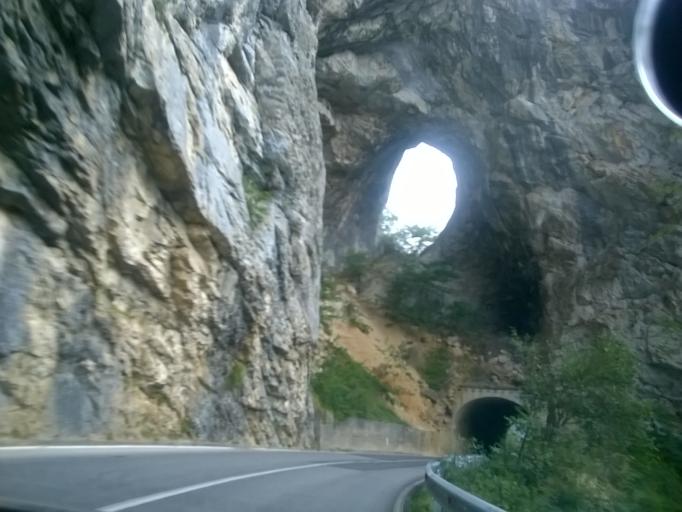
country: ME
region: Opstina Pluzine
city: Pluzine
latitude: 43.2315
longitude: 18.8458
